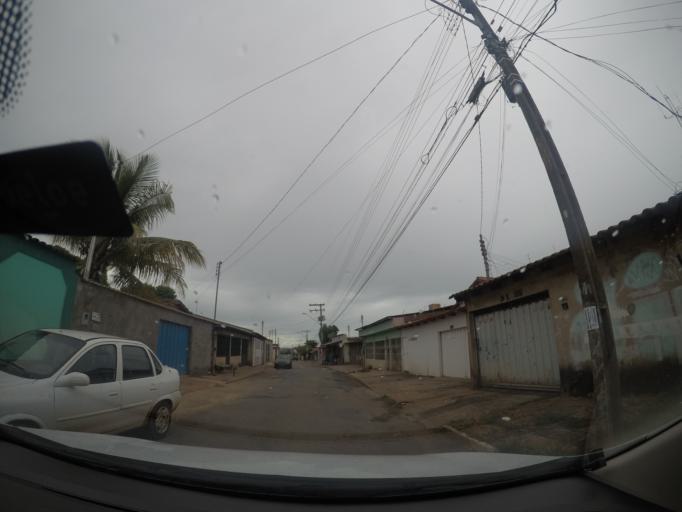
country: BR
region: Goias
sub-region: Goiania
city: Goiania
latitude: -16.6488
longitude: -49.3199
